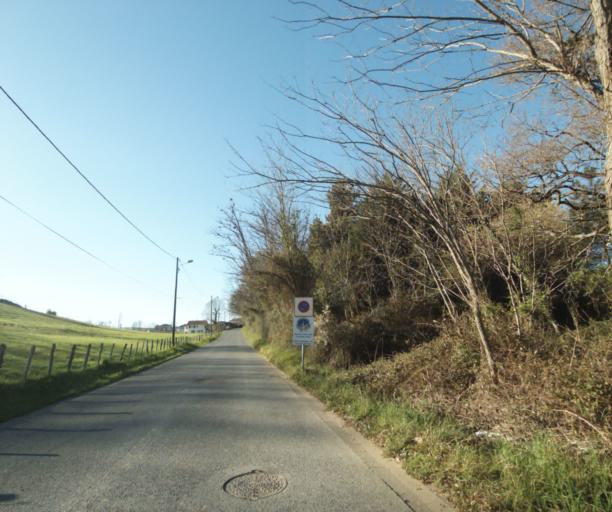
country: FR
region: Aquitaine
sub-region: Departement des Pyrenees-Atlantiques
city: Hendaye
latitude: 43.3600
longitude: -1.7537
